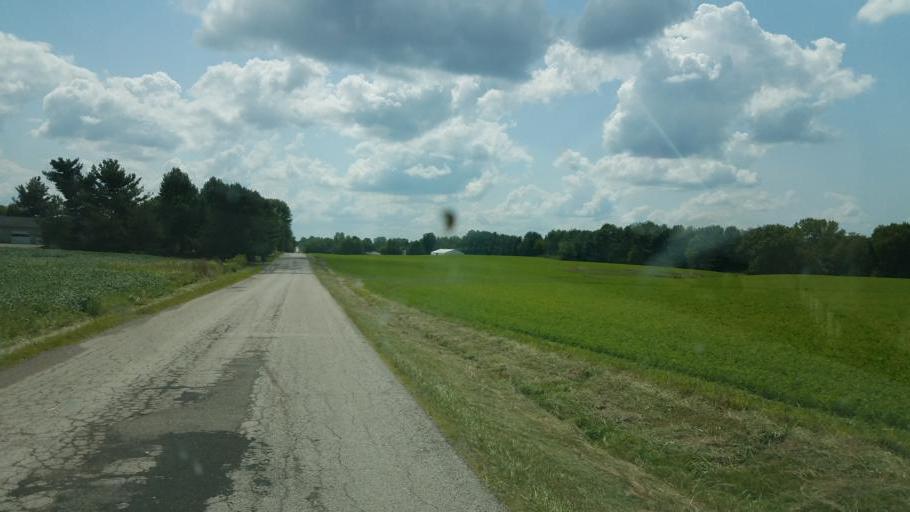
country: US
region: Ohio
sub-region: Knox County
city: Centerburg
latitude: 40.3714
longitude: -82.8032
